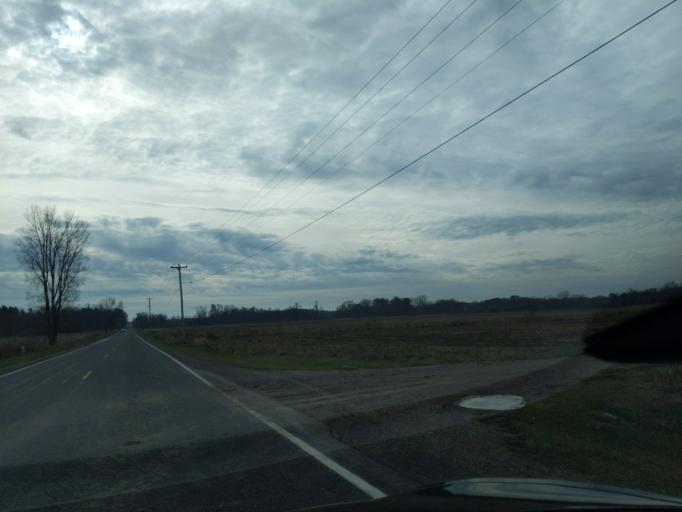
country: US
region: Michigan
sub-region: Ingham County
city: Leslie
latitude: 42.4920
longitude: -84.5217
